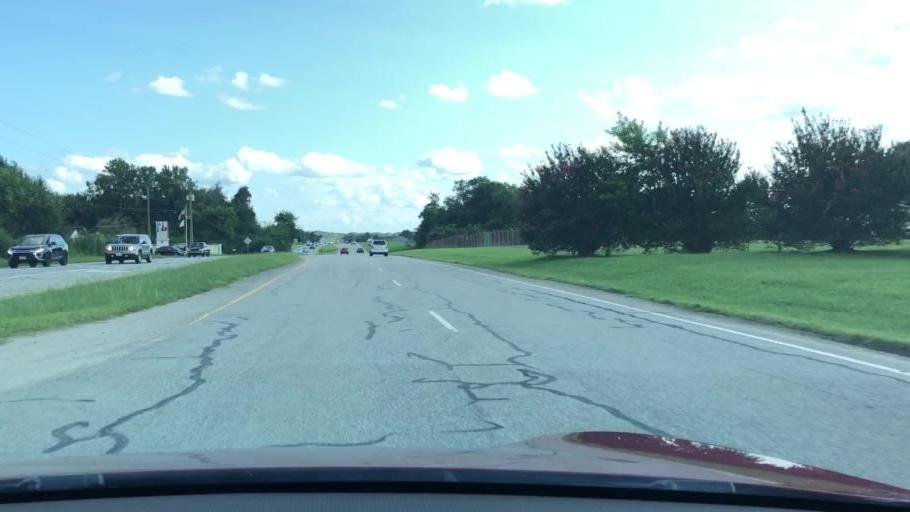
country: US
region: Virginia
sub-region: City of Virginia Beach
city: Virginia Beach
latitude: 36.8279
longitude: -76.0104
